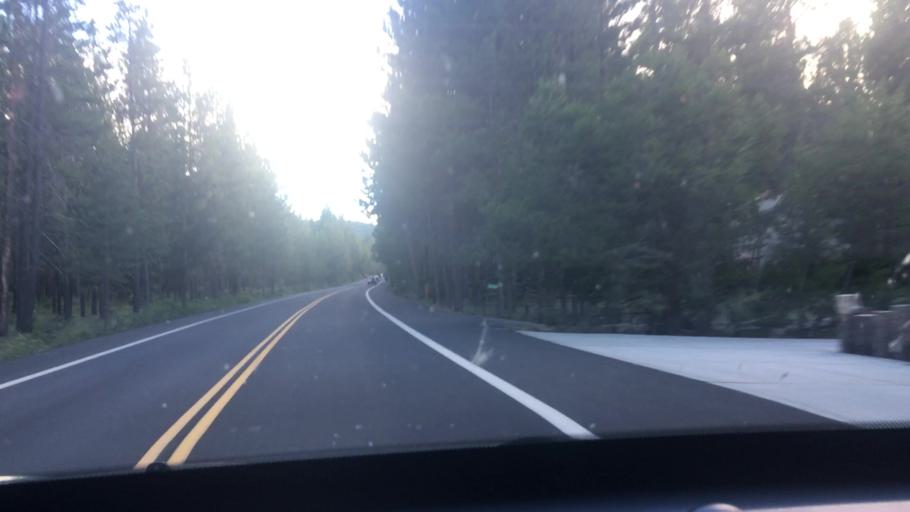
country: US
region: Oregon
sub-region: Deschutes County
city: Deschutes River Woods
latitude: 44.0359
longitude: -121.5061
